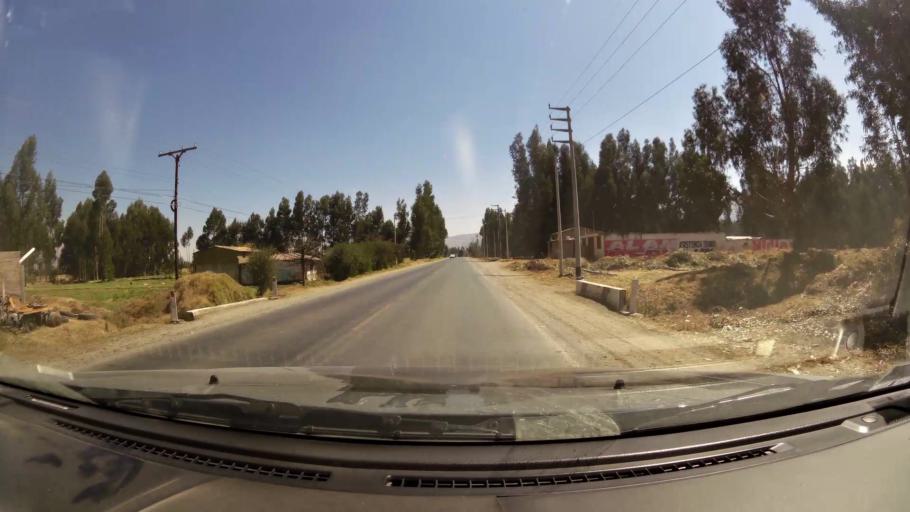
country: PE
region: Junin
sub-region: Provincia de Jauja
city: San Lorenzo
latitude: -11.8632
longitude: -75.3742
